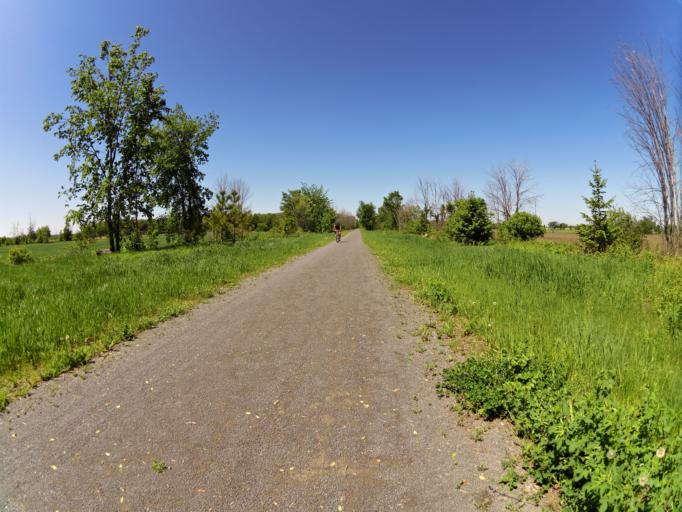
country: CA
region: Ontario
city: Clarence-Rockland
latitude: 45.4175
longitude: -75.3902
